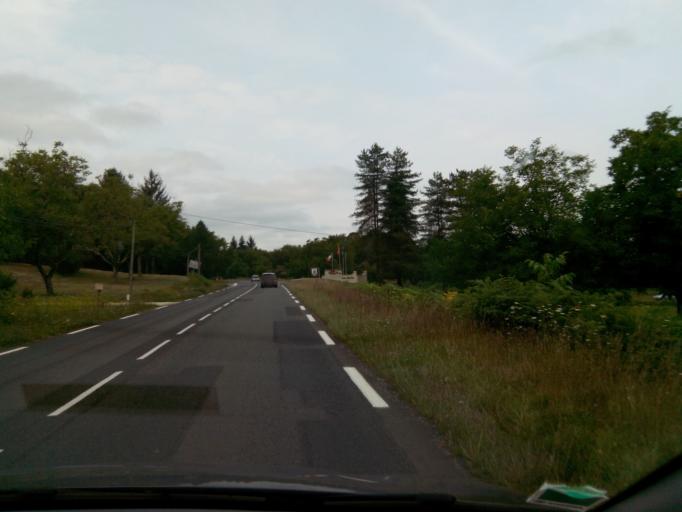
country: FR
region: Aquitaine
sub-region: Departement de la Dordogne
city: Carsac-Aillac
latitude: 44.8618
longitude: 1.2955
